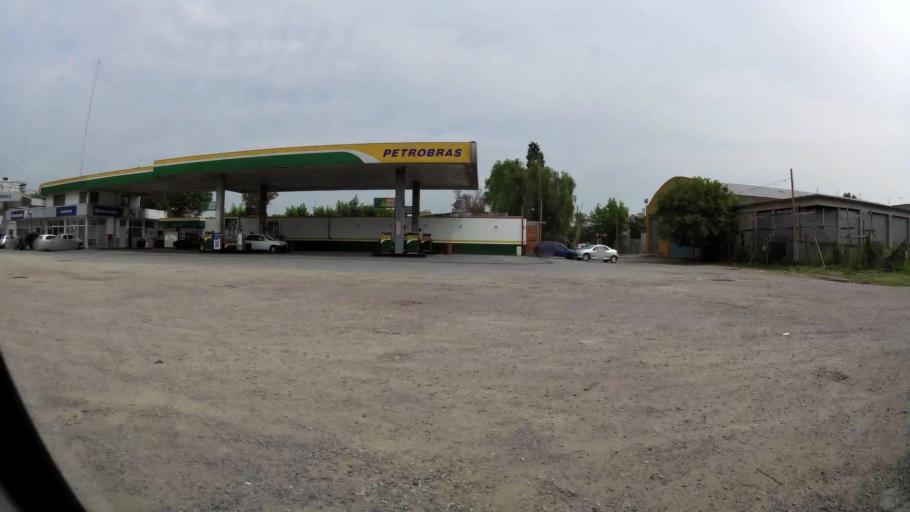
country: AR
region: Buenos Aires
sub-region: Partido de La Plata
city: La Plata
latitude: -34.9007
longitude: -57.9941
